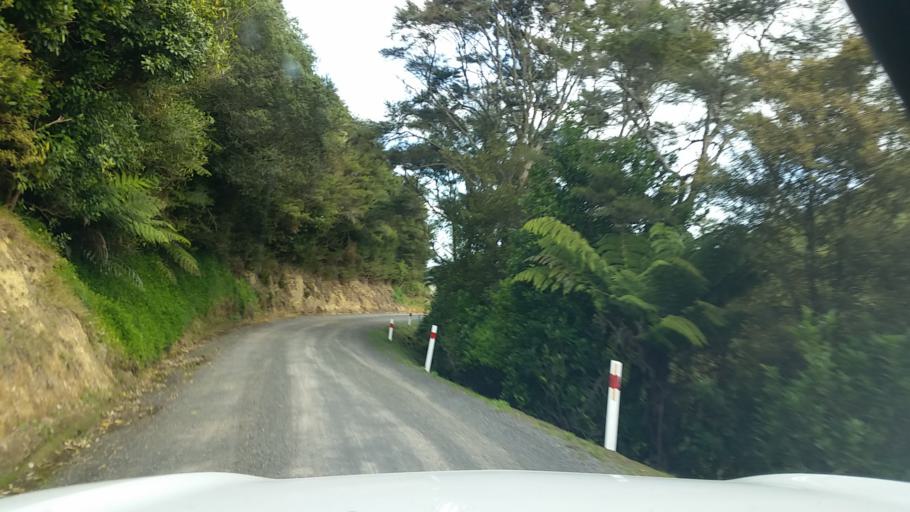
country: NZ
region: Waikato
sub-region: Hauraki District
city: Ngatea
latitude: -37.4810
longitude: 175.4525
